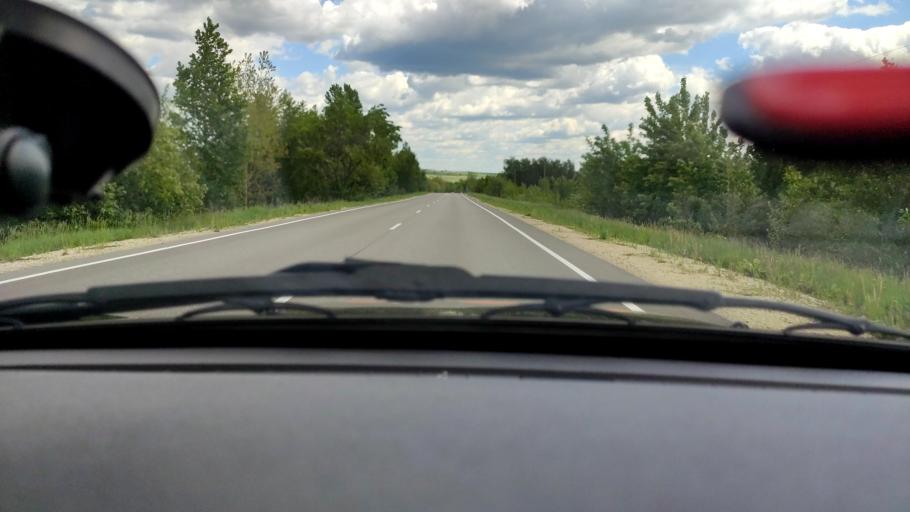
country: RU
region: Belgorod
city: Krasnoye
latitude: 51.0681
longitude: 38.7998
